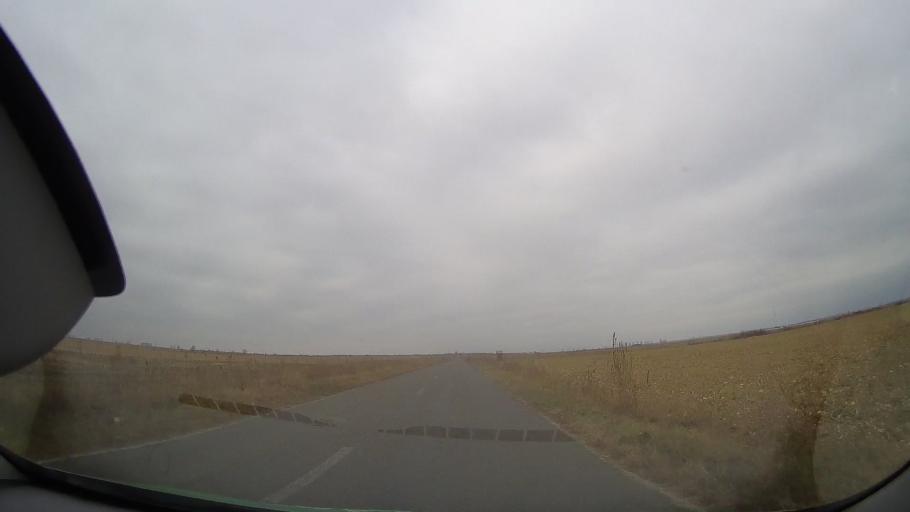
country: RO
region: Buzau
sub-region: Comuna Luciu
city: Luciu
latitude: 44.9751
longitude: 27.0653
